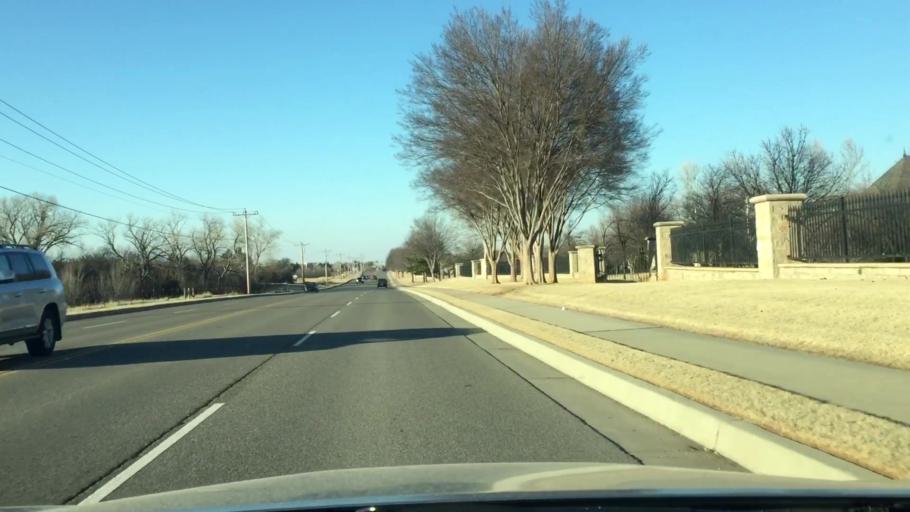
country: US
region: Oklahoma
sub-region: Oklahoma County
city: The Village
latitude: 35.6174
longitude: -97.6207
